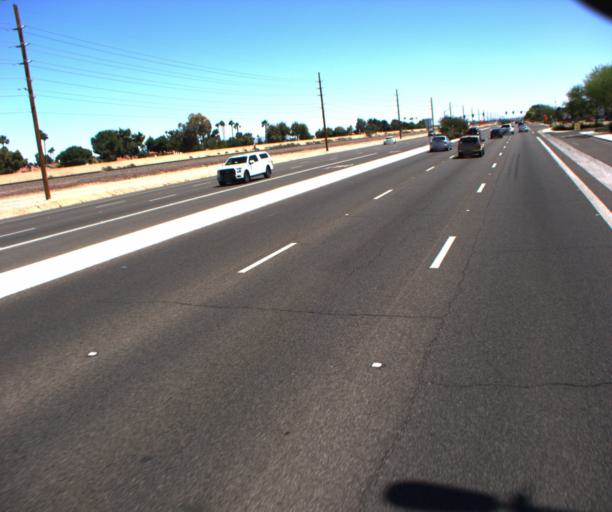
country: US
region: Arizona
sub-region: Maricopa County
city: Sun City West
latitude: 33.6510
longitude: -112.3663
